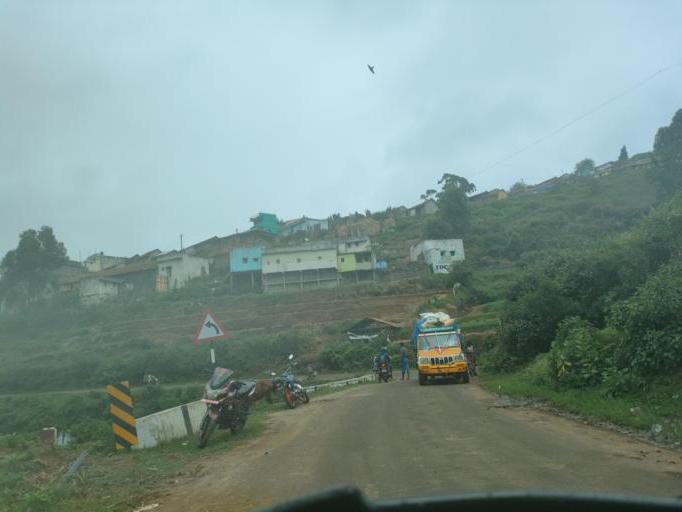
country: IN
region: Tamil Nadu
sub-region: Dindigul
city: Kodaikanal
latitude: 10.2232
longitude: 77.3468
